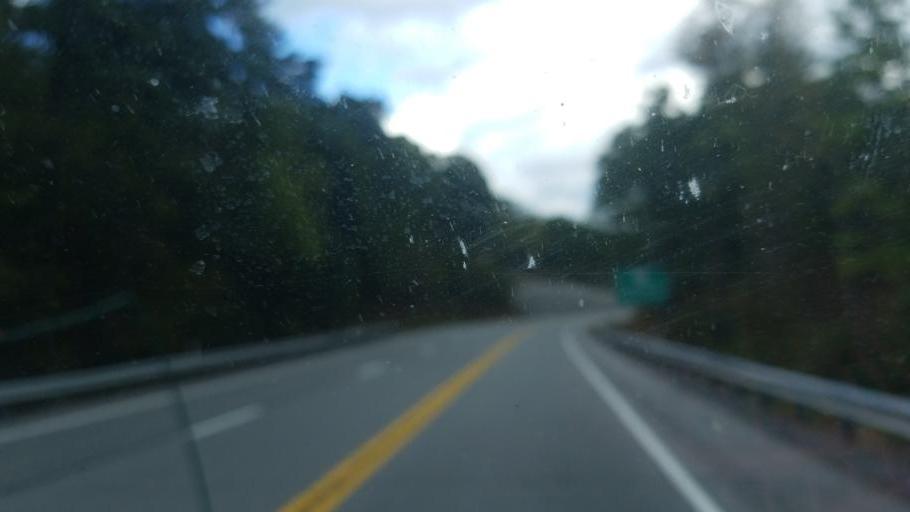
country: US
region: Pennsylvania
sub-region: Fulton County
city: McConnellsburg
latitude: 39.9424
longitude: -78.0121
